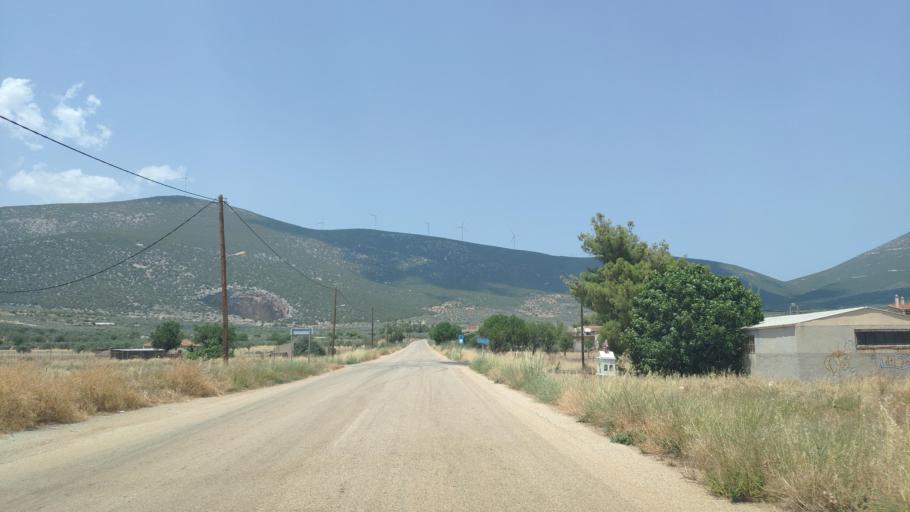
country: GR
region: Peloponnese
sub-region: Nomos Argolidos
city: Didyma
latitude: 37.4605
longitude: 23.1685
